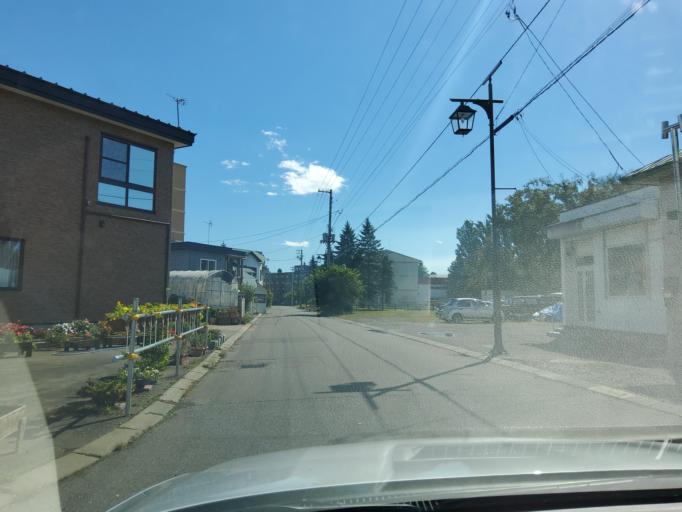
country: JP
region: Hokkaido
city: Obihiro
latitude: 42.9332
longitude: 143.2995
